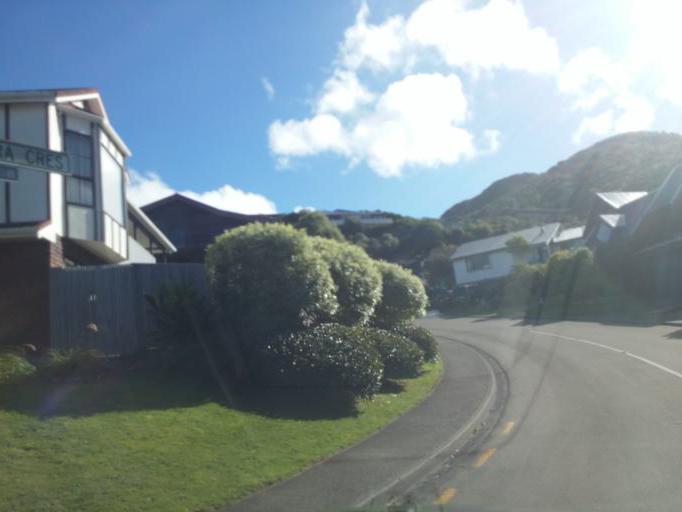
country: NZ
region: Wellington
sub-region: Wellington City
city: Kelburn
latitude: -41.2432
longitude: 174.7808
